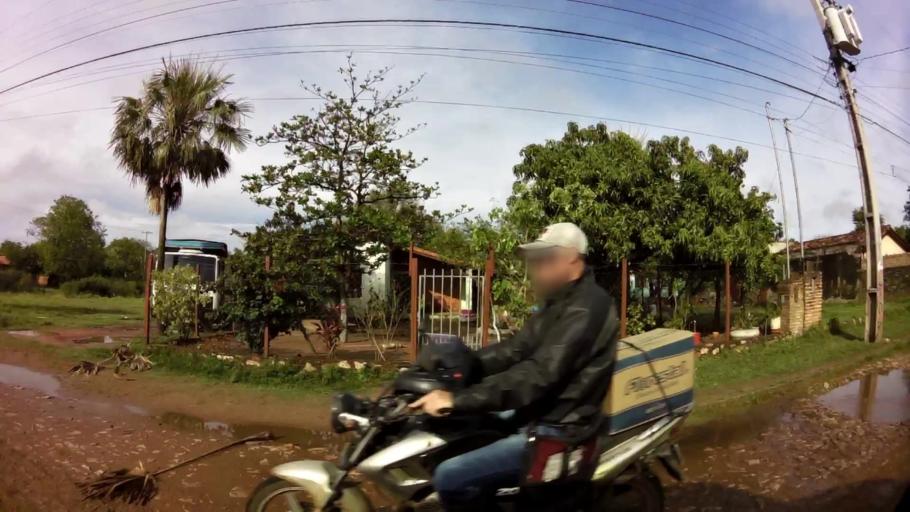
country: PY
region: Central
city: Limpio
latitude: -25.1856
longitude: -57.4877
